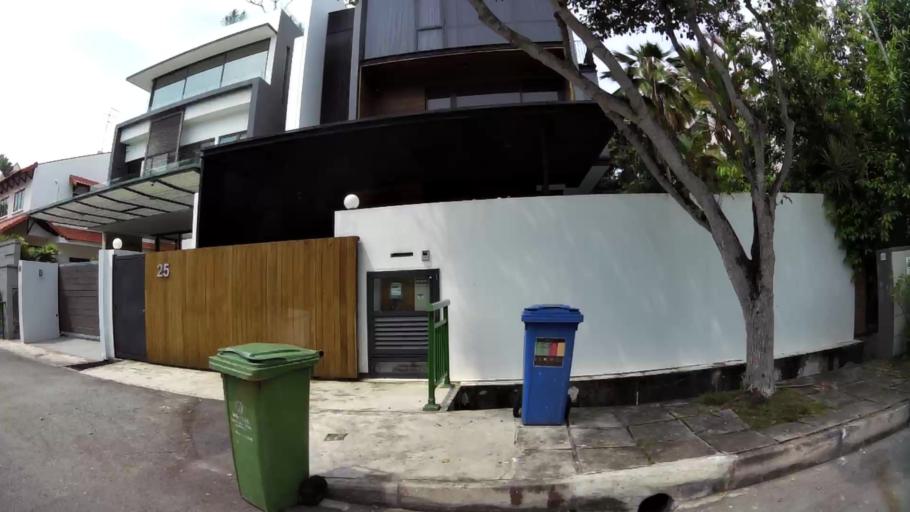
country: MY
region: Johor
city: Kampung Pasir Gudang Baru
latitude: 1.3818
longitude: 103.9458
